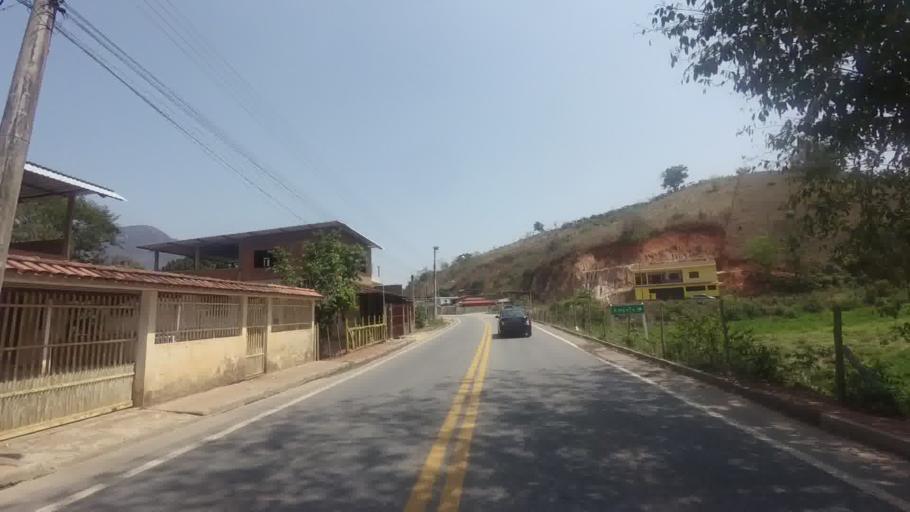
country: BR
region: Espirito Santo
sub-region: Mimoso Do Sul
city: Mimoso do Sul
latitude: -20.9404
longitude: -41.3305
